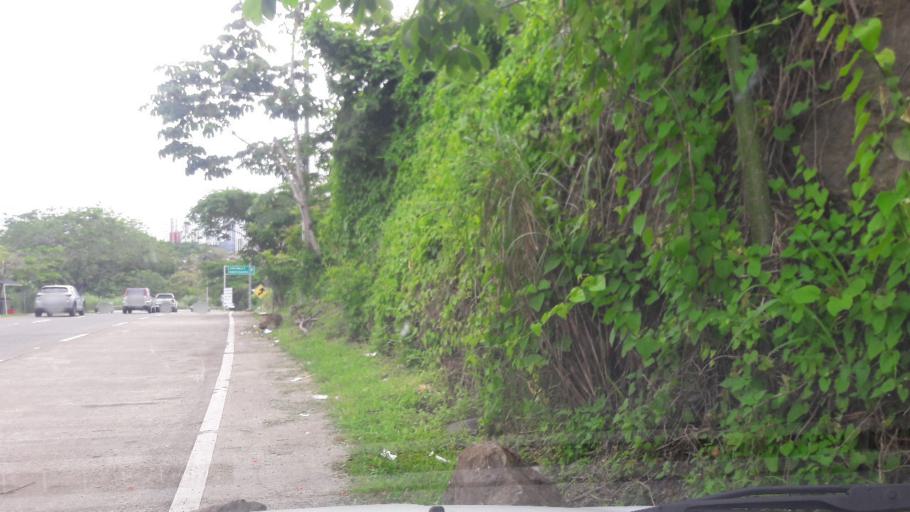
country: PA
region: Panama
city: Panama
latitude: 9.0044
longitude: -79.5431
